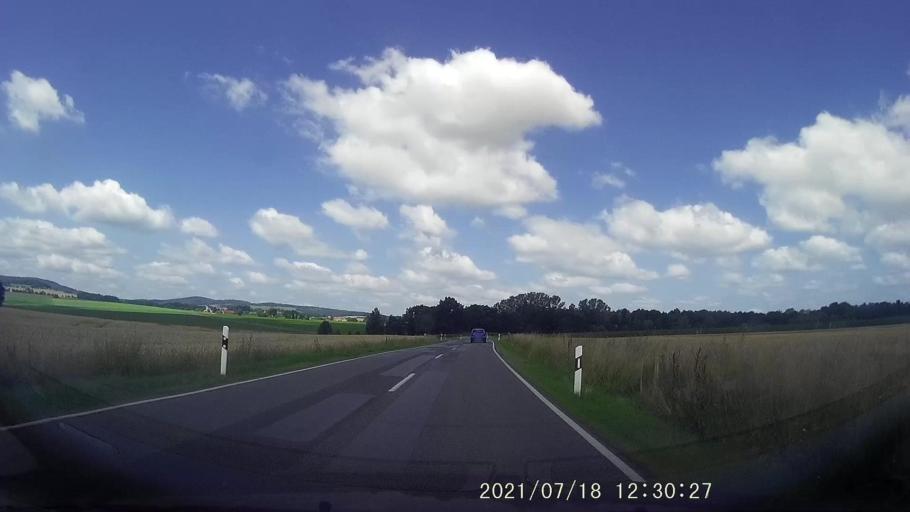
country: DE
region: Saxony
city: Konigshain
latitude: 51.1722
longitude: 14.9096
